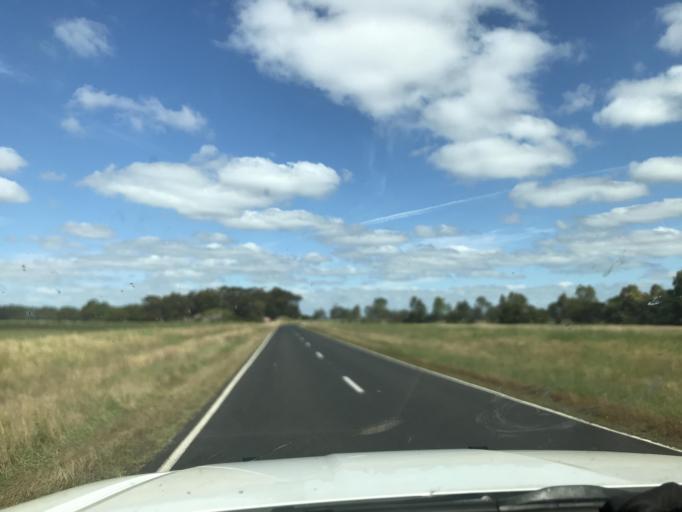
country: AU
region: South Australia
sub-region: Naracoorte and Lucindale
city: Naracoorte
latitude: -37.0187
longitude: 141.3030
